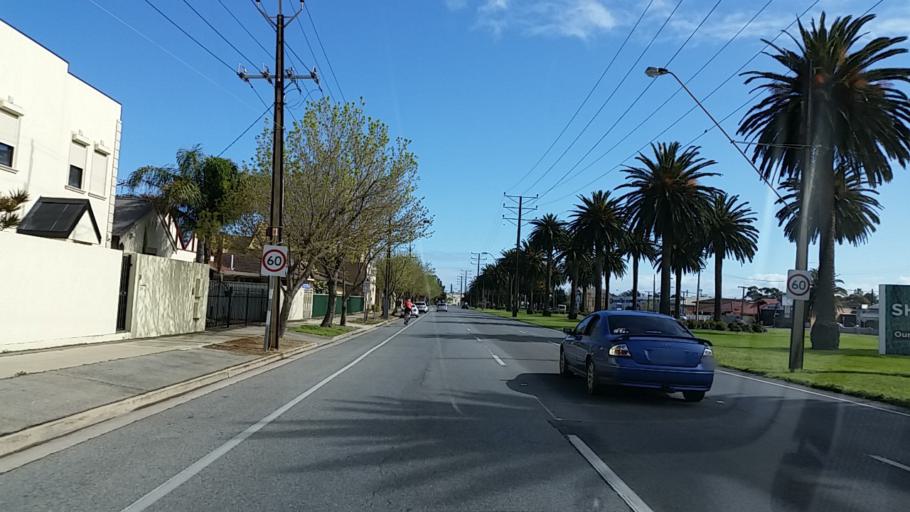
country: AU
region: South Australia
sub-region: Port Adelaide Enfield
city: Alberton
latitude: -34.8581
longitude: 138.5116
